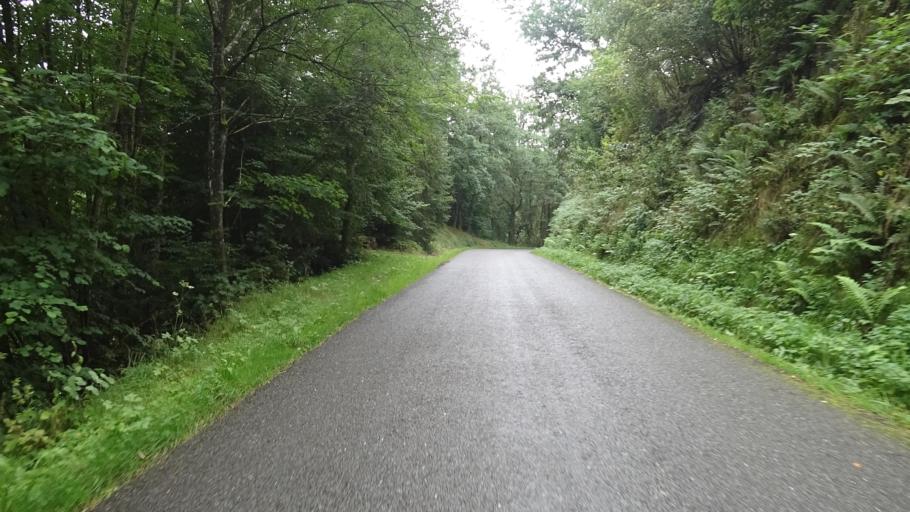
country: BE
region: Wallonia
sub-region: Province du Luxembourg
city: Chiny
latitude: 49.7895
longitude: 5.3750
